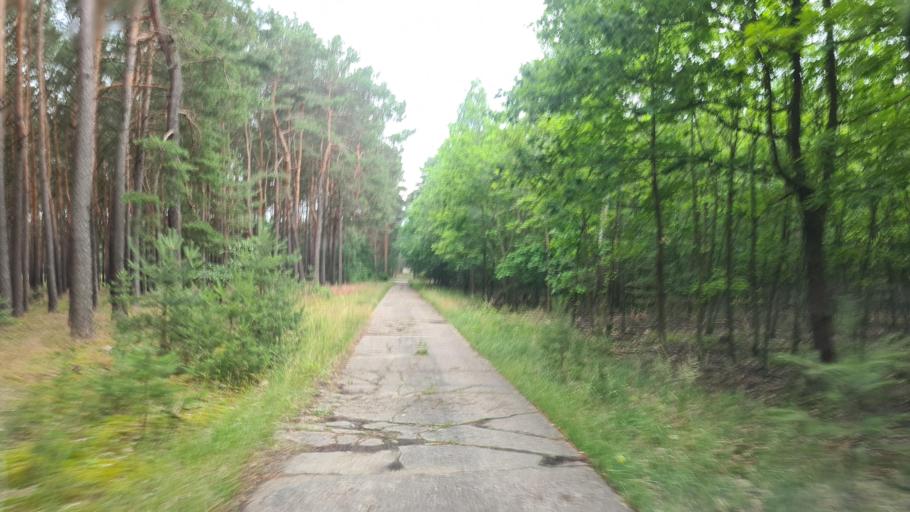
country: DE
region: Brandenburg
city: Crinitz
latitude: 51.7179
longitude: 13.7140
